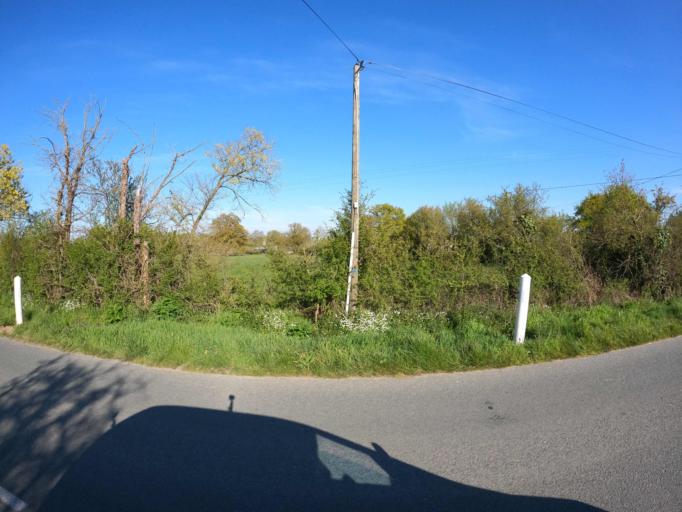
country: FR
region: Pays de la Loire
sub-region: Departement de la Vendee
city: Beaurepaire
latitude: 46.9230
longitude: -1.1166
